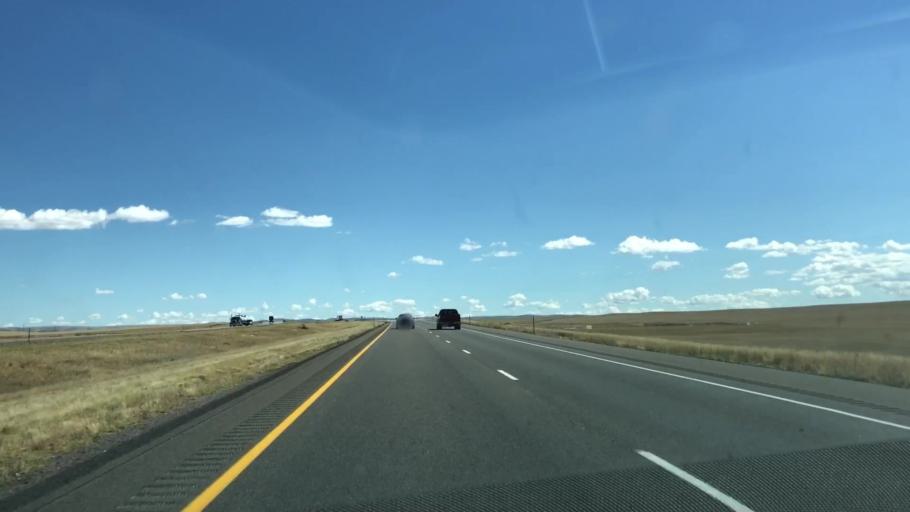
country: US
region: Wyoming
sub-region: Albany County
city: Laramie
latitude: 41.3558
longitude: -105.7484
